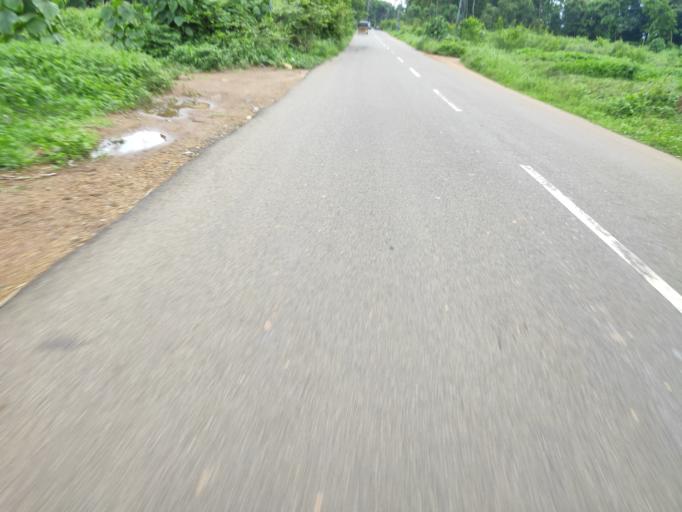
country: IN
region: Kerala
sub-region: Malappuram
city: Manjeri
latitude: 11.2228
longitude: 76.2647
